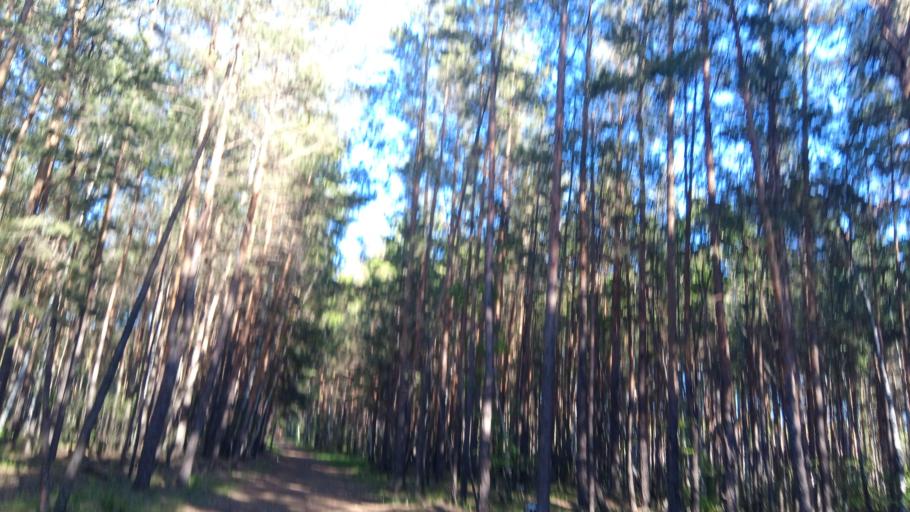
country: RU
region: Chelyabinsk
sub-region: Gorod Chelyabinsk
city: Chelyabinsk
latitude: 55.1335
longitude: 61.3361
